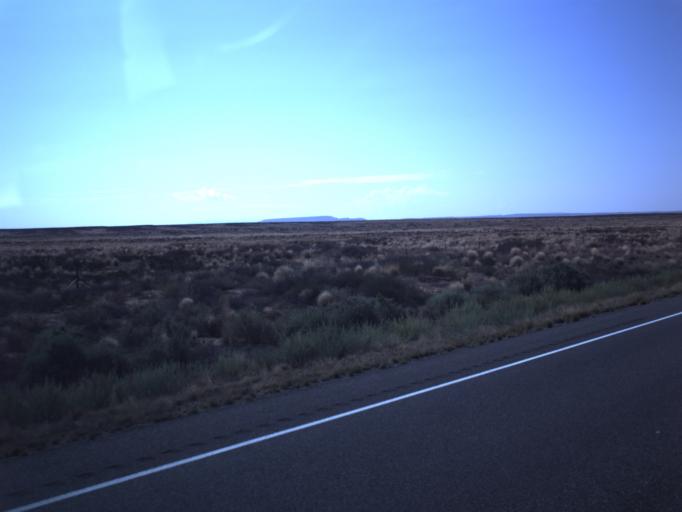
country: US
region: Utah
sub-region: San Juan County
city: Blanding
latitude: 37.3286
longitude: -109.5208
